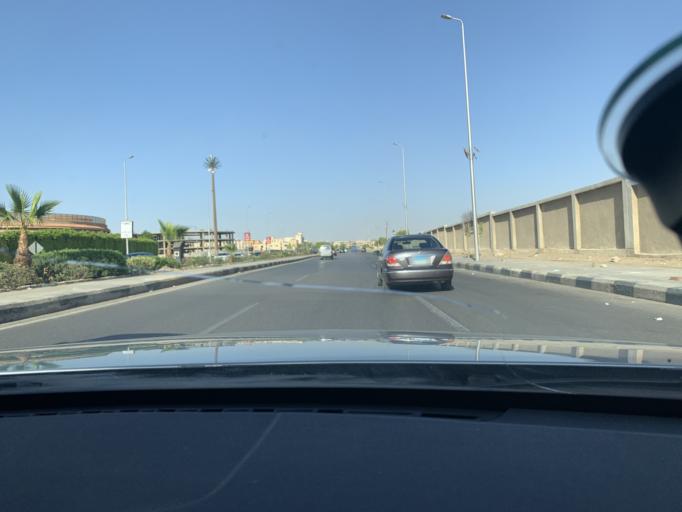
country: EG
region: Muhafazat al Qalyubiyah
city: Al Khankah
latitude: 30.0530
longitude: 31.4342
